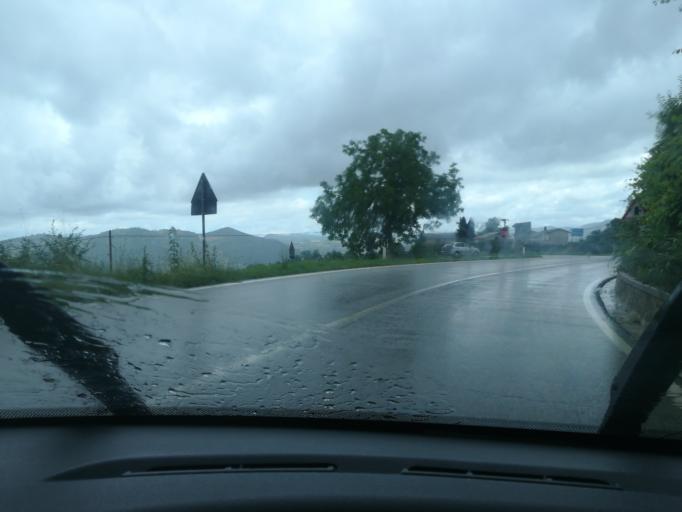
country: IT
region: The Marches
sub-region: Province of Fermo
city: Amandola
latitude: 42.9966
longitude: 13.3396
